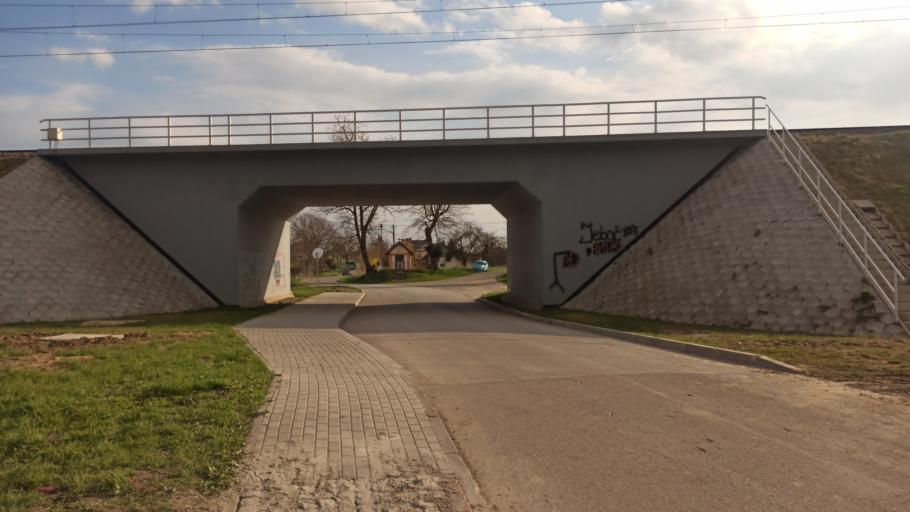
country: PL
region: Subcarpathian Voivodeship
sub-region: Powiat jaroslawski
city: Radymno
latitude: 49.9447
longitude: 22.8140
